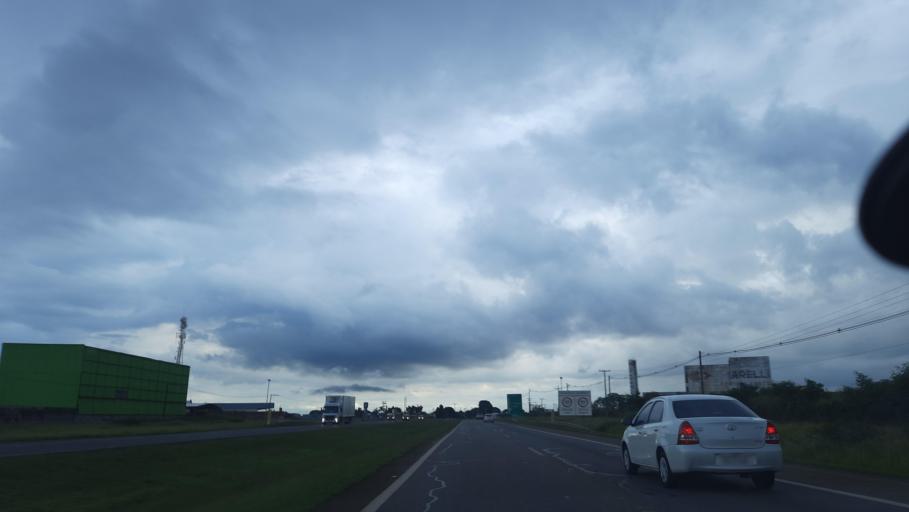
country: BR
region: Sao Paulo
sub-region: Moji-Guacu
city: Mogi-Gaucu
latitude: -22.3424
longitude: -46.9573
